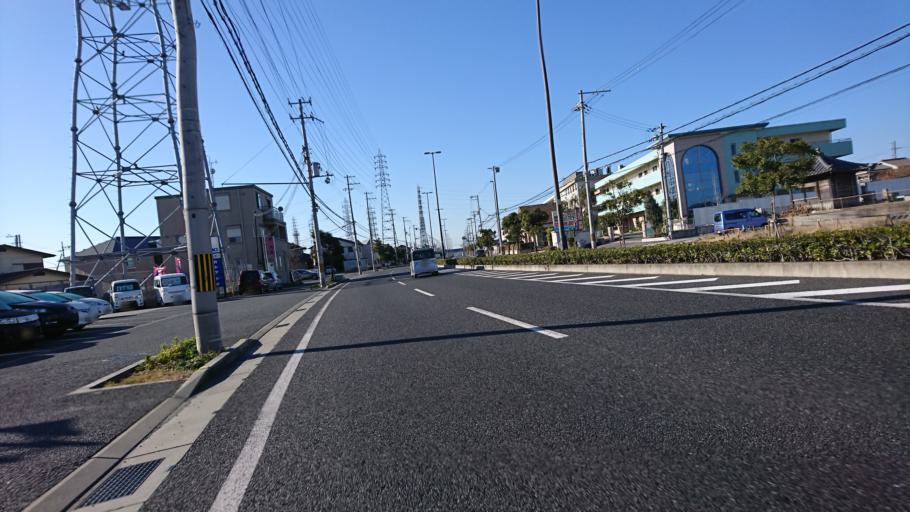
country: JP
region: Hyogo
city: Kakogawacho-honmachi
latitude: 34.7729
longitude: 134.8106
